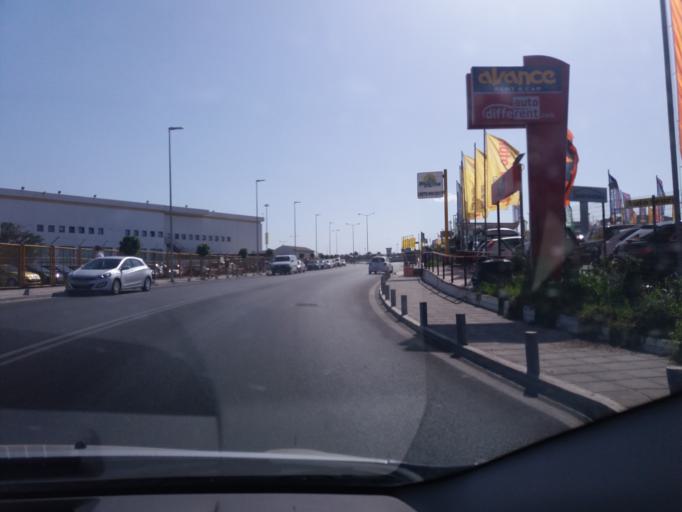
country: GR
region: Crete
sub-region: Nomos Irakleiou
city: Nea Alikarnassos
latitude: 35.3378
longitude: 25.1715
